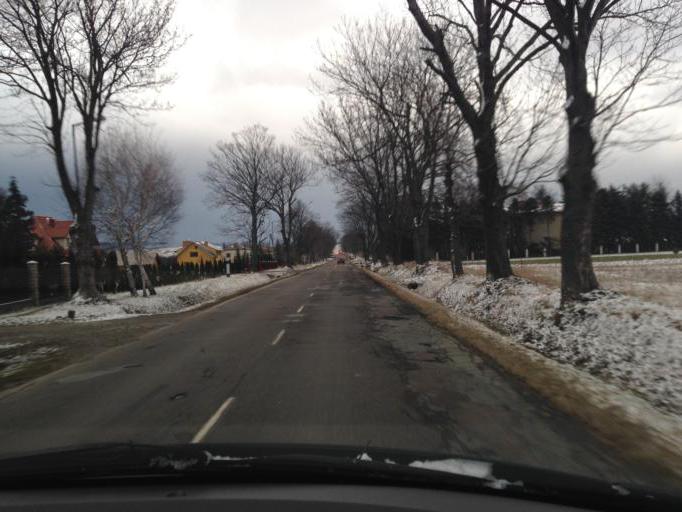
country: PL
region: Subcarpathian Voivodeship
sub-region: Powiat jasielski
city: Osiek Jasielski
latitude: 49.6118
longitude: 21.4628
